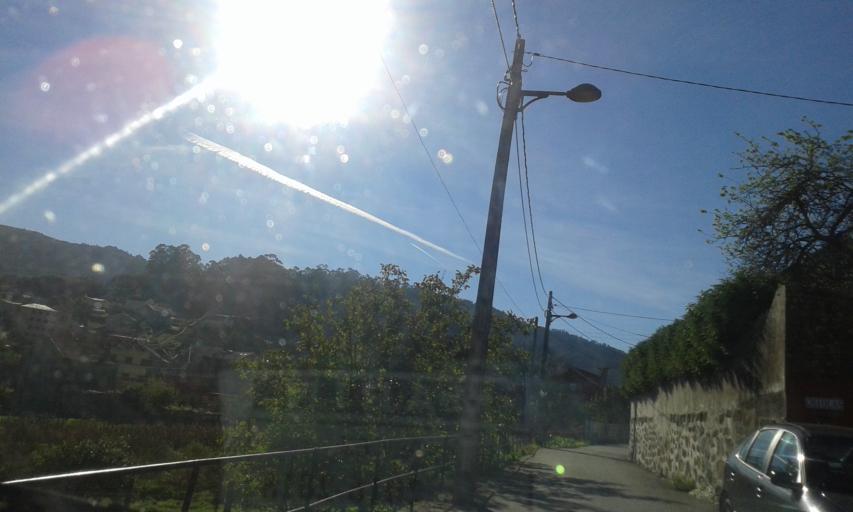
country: ES
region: Galicia
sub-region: Provincia de Pontevedra
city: Marin
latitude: 42.3579
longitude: -8.7425
